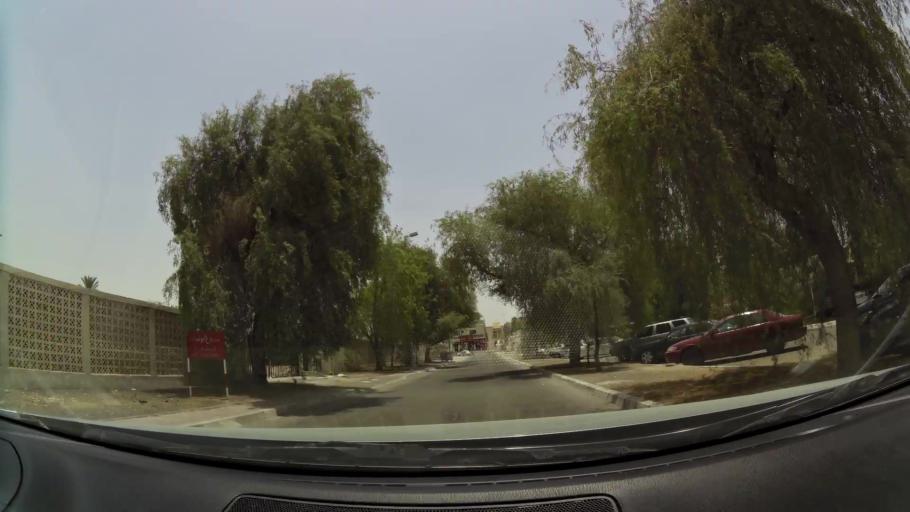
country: AE
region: Abu Dhabi
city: Al Ain
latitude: 24.2127
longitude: 55.7550
